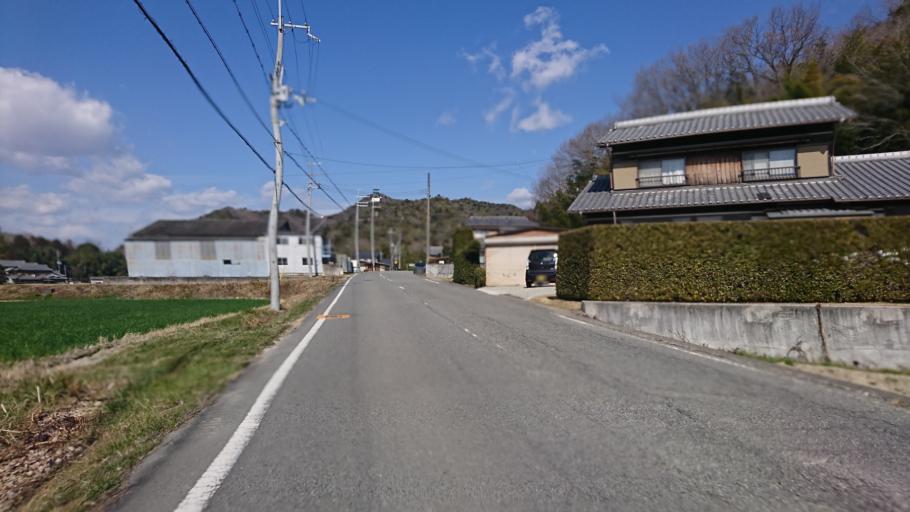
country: JP
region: Hyogo
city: Kakogawacho-honmachi
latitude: 34.8515
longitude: 134.8103
